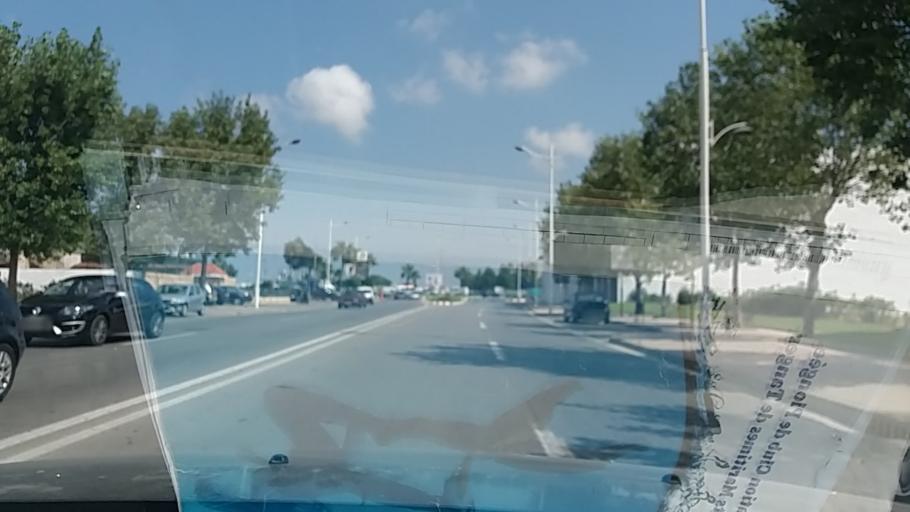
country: MA
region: Tanger-Tetouan
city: Tetouan
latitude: 35.5828
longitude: -5.3333
